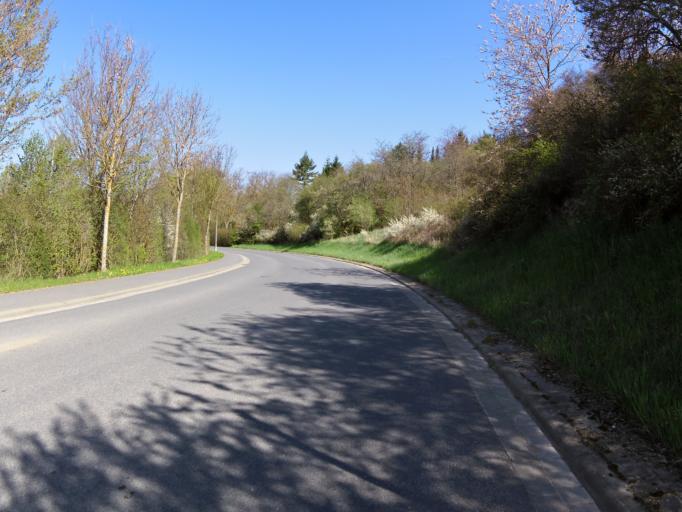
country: DE
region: Bavaria
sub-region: Regierungsbezirk Unterfranken
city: Rottendorf
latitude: 49.7961
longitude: 10.0320
